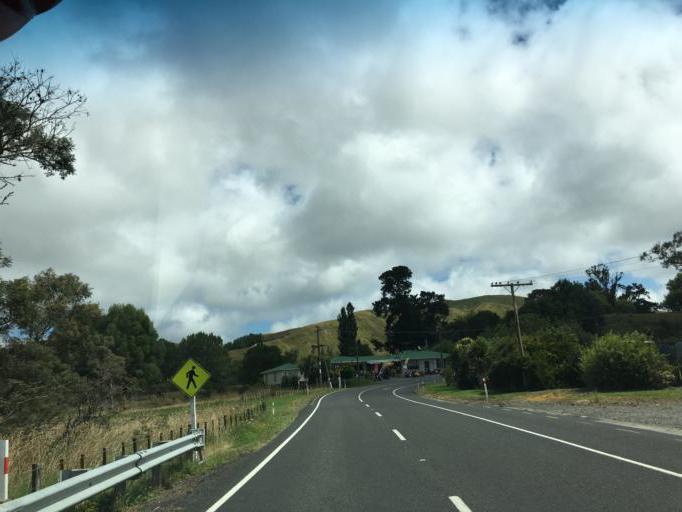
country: NZ
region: Hawke's Bay
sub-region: Napier City
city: Napier
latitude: -39.1322
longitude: 177.0049
